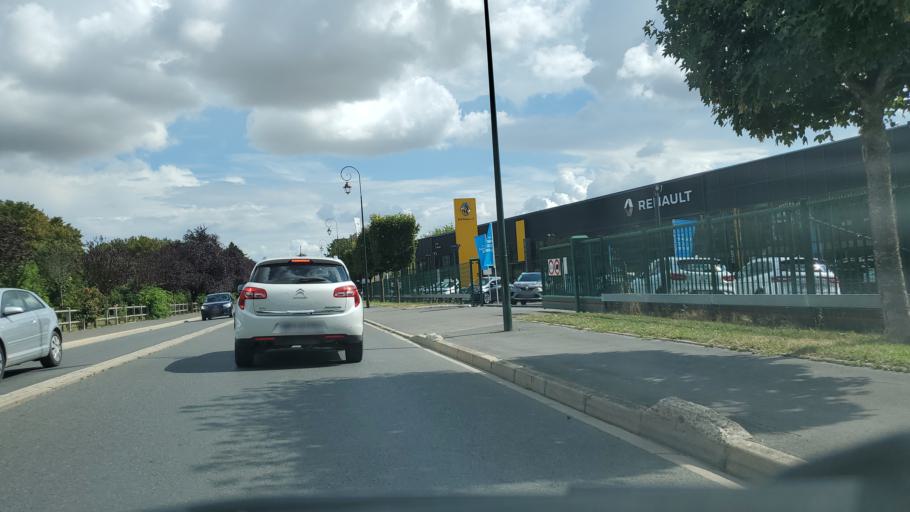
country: FR
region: Ile-de-France
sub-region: Departement de Seine-et-Marne
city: Coulommiers
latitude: 48.8101
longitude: 3.0800
